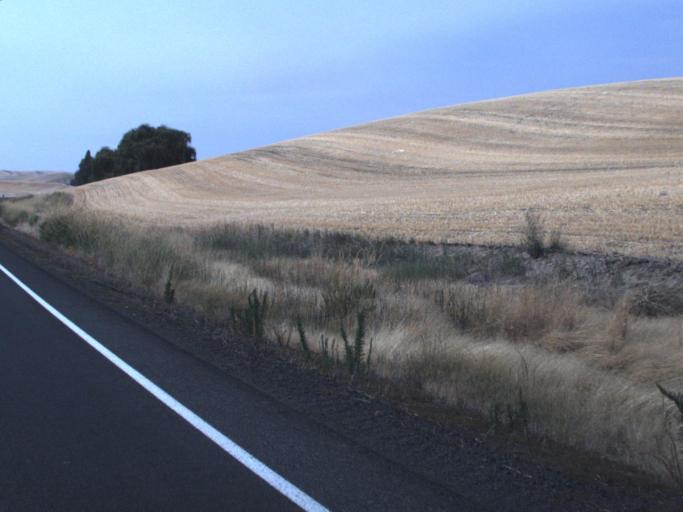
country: US
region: Washington
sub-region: Whitman County
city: Pullman
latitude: 46.8000
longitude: -117.1316
